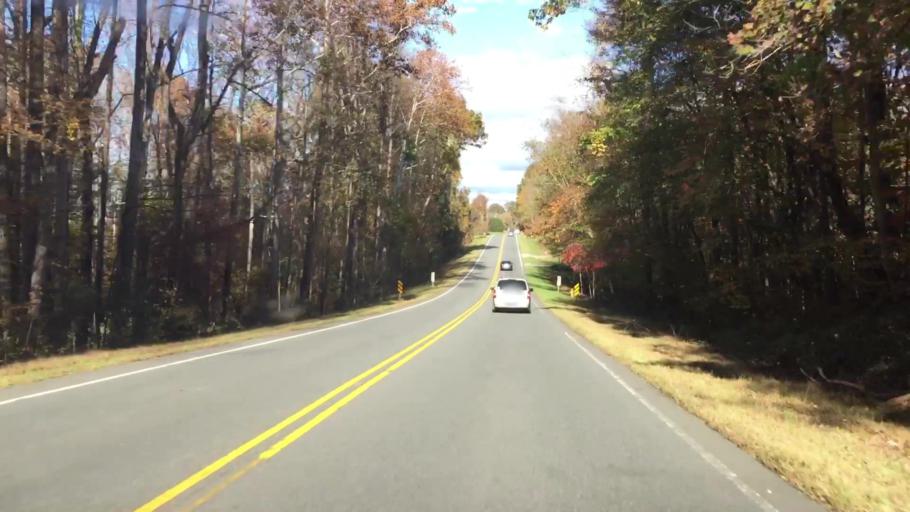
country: US
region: North Carolina
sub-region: Forsyth County
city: Kernersville
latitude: 36.2082
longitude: -80.0709
